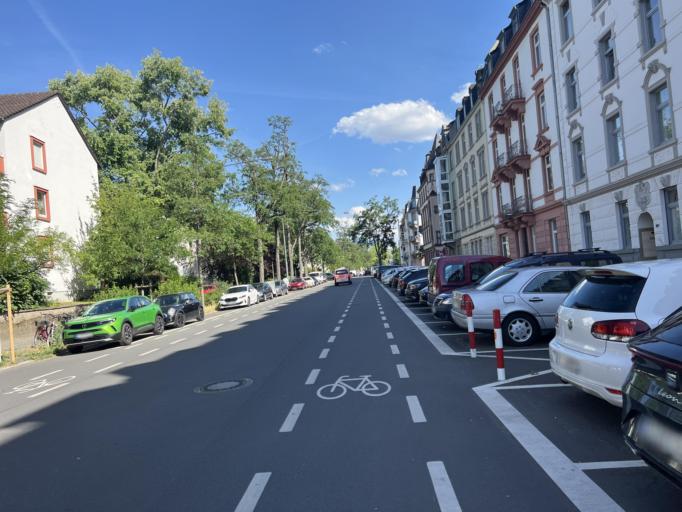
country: DE
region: Hesse
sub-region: Regierungsbezirk Darmstadt
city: Frankfurt am Main
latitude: 50.1268
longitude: 8.6437
